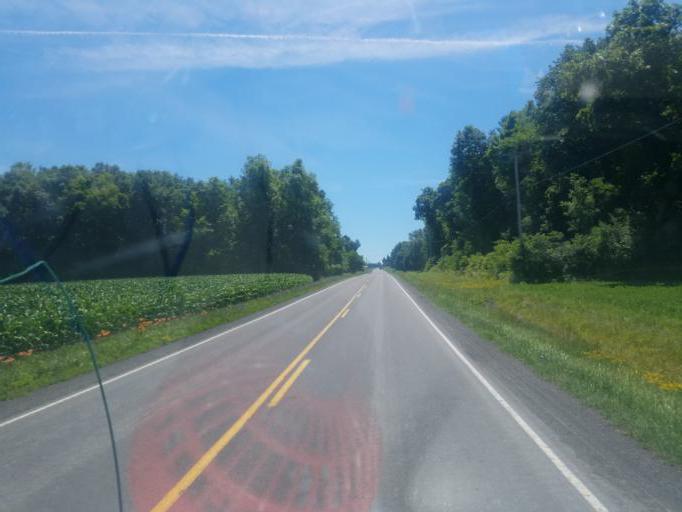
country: US
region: New York
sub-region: Yates County
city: Penn Yan
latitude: 42.6277
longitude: -76.9991
